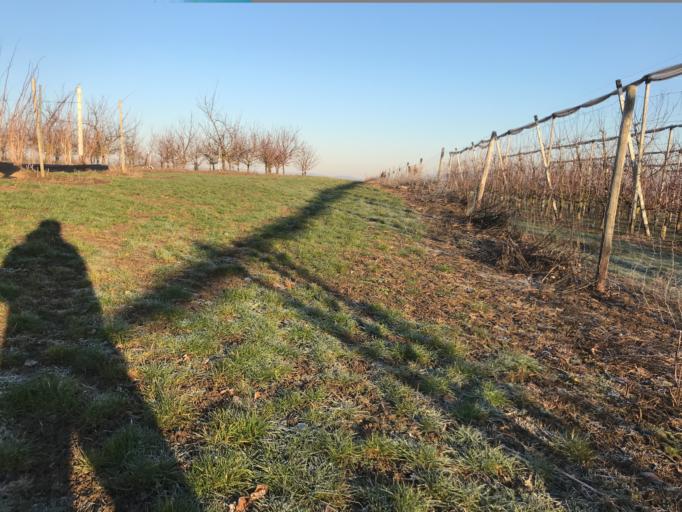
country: DE
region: Rheinland-Pfalz
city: Budenheim
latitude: 49.9840
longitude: 8.1936
